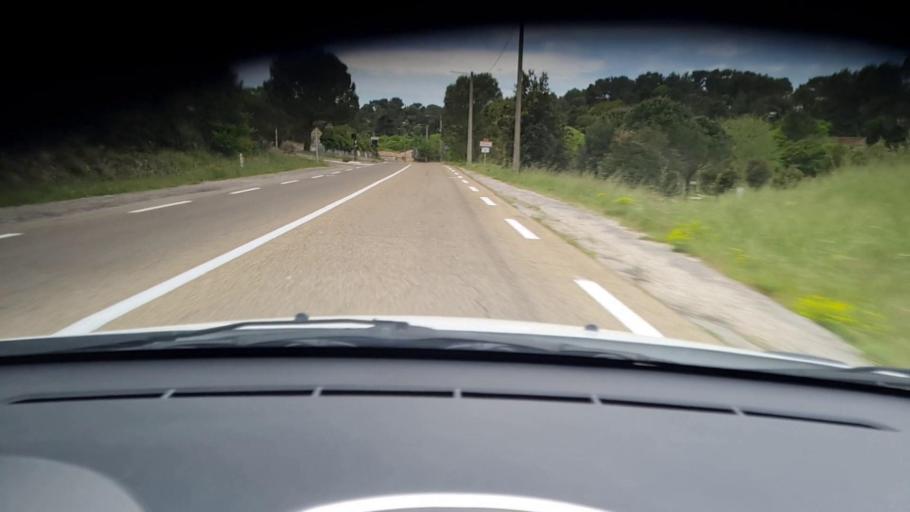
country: FR
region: Languedoc-Roussillon
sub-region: Departement du Gard
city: Nimes
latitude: 43.8641
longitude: 4.3778
